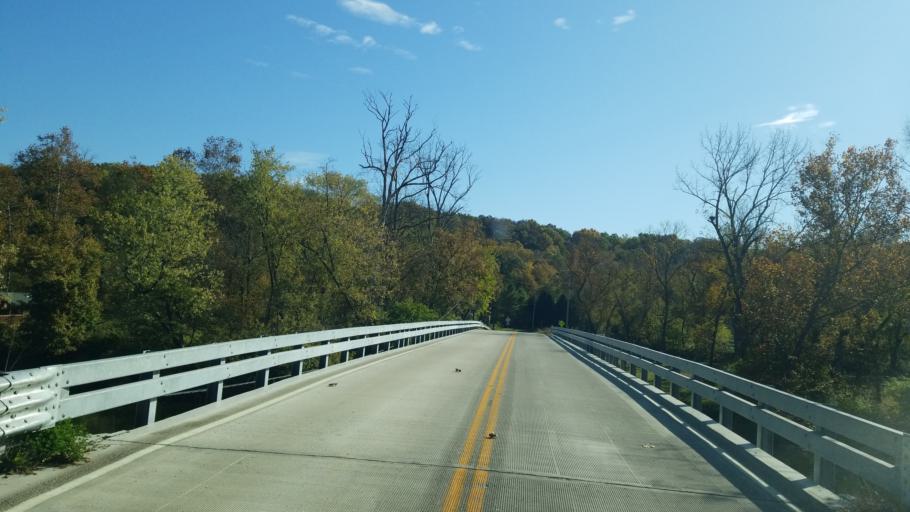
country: US
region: Ohio
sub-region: Warren County
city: Morrow
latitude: 39.3787
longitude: -84.0931
